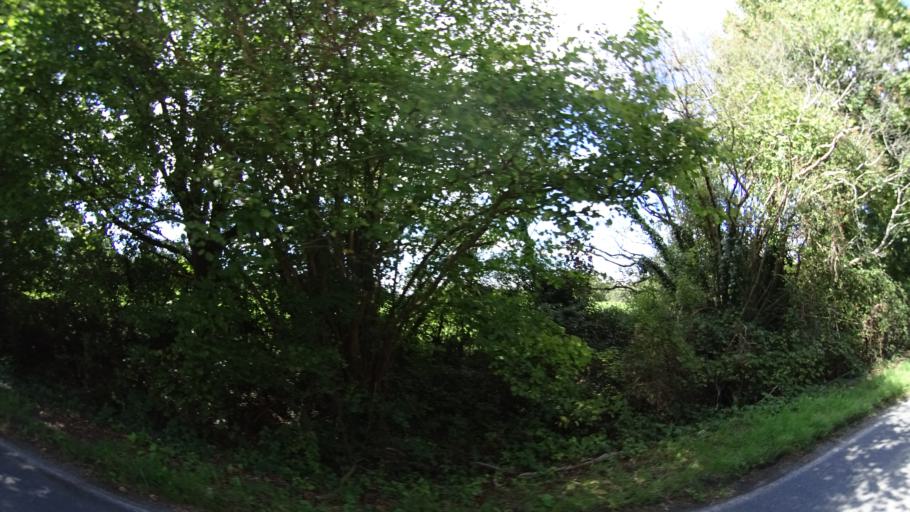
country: GB
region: England
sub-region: Hampshire
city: Romsey
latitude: 51.0098
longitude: -1.4719
